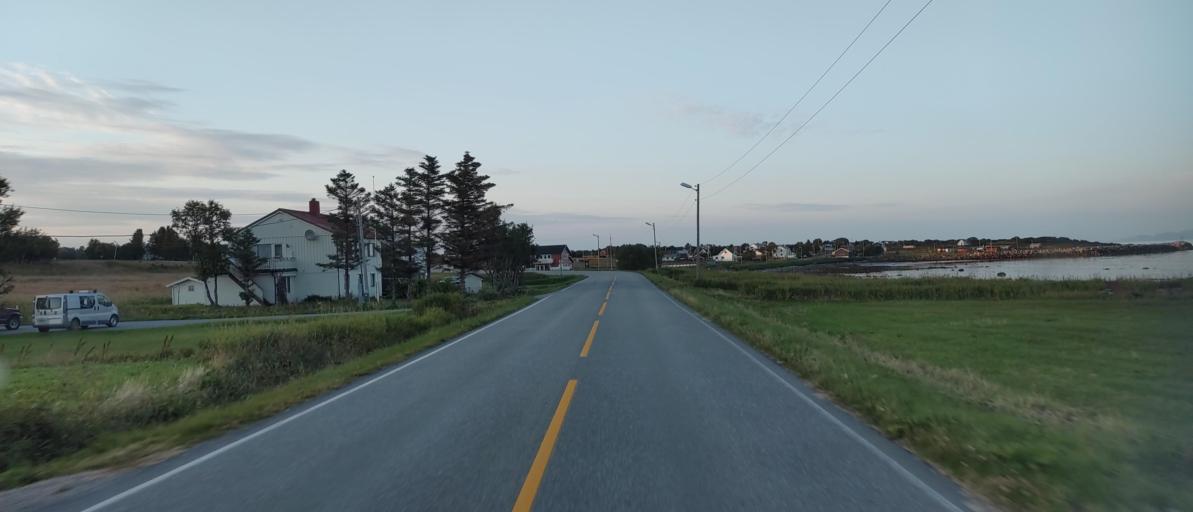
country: NO
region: Nordland
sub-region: Andoy
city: Andenes
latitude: 69.2430
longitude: 16.1171
